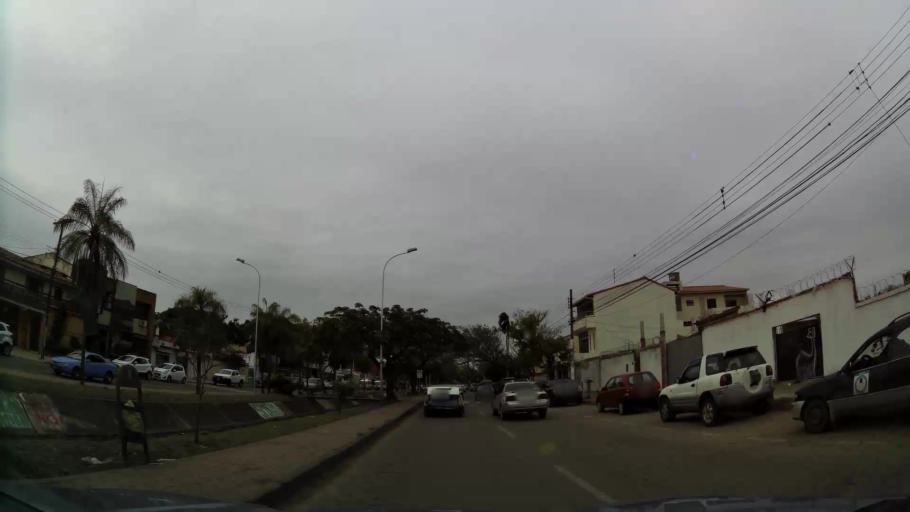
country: BO
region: Santa Cruz
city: Santa Cruz de la Sierra
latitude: -17.7936
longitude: -63.2026
